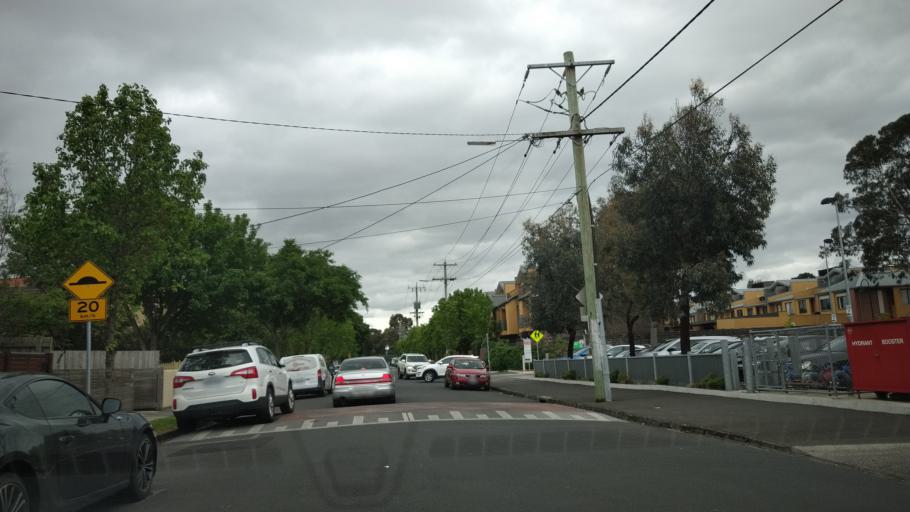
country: AU
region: Victoria
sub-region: Glen Eira
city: Glen Huntly
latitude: -37.8886
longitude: 145.0408
